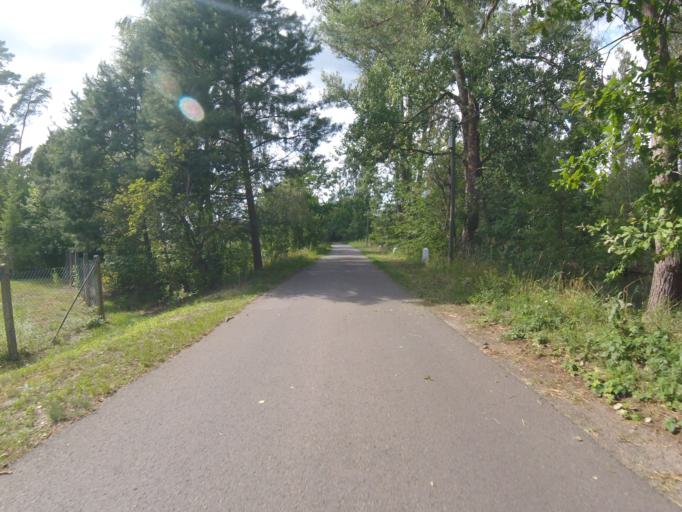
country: DE
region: Brandenburg
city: Halbe
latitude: 52.0984
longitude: 13.7756
